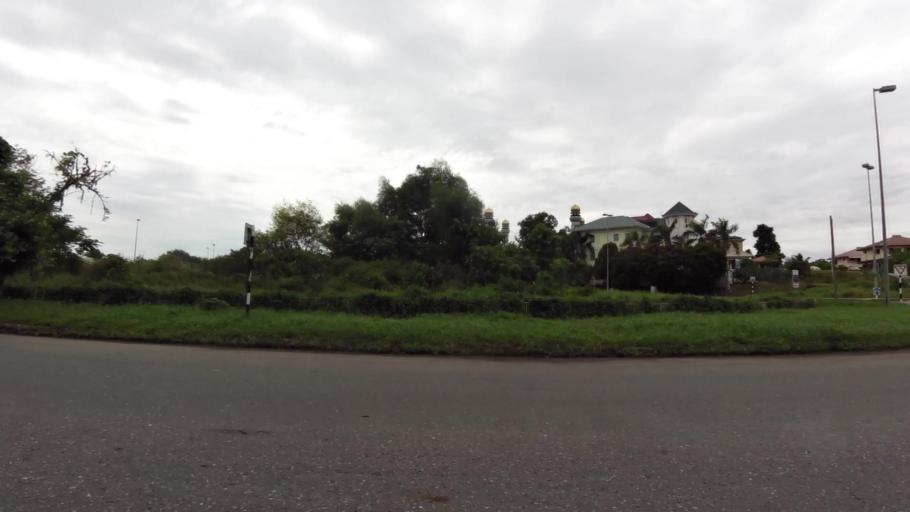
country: BN
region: Brunei and Muara
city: Bandar Seri Begawan
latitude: 4.8985
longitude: 114.9187
